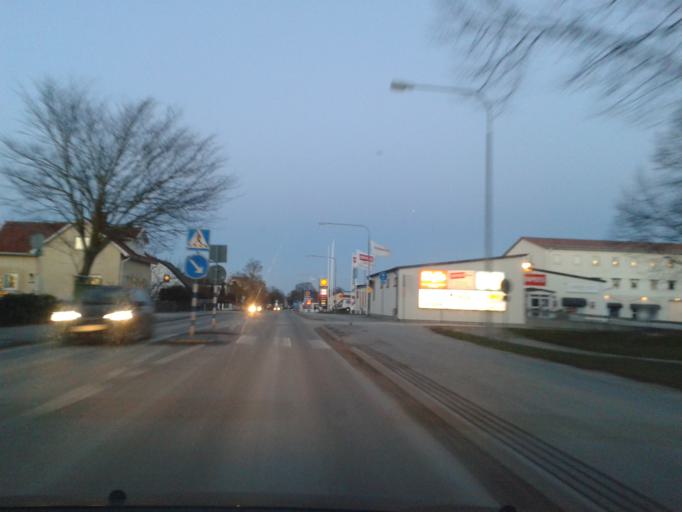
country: SE
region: Gotland
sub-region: Gotland
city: Visby
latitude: 57.6286
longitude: 18.2849
